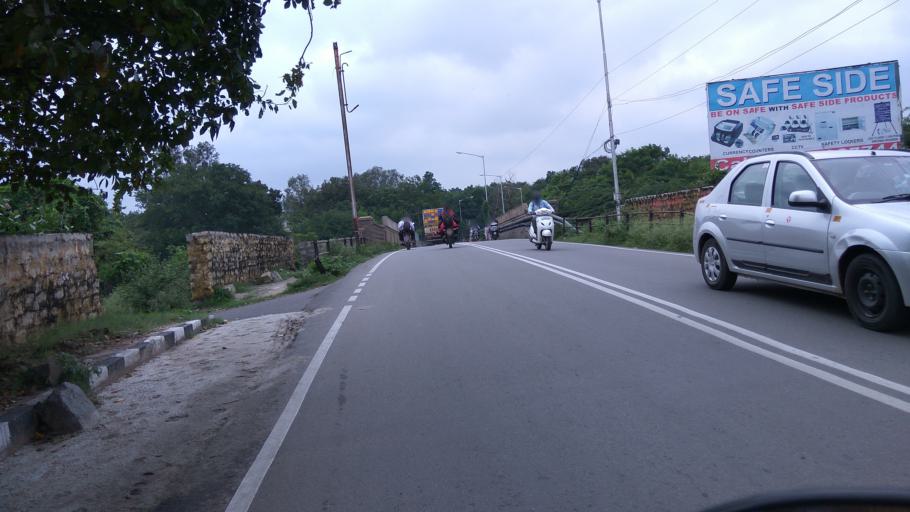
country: IN
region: Telangana
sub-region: Hyderabad
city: Malkajgiri
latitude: 17.4389
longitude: 78.5250
